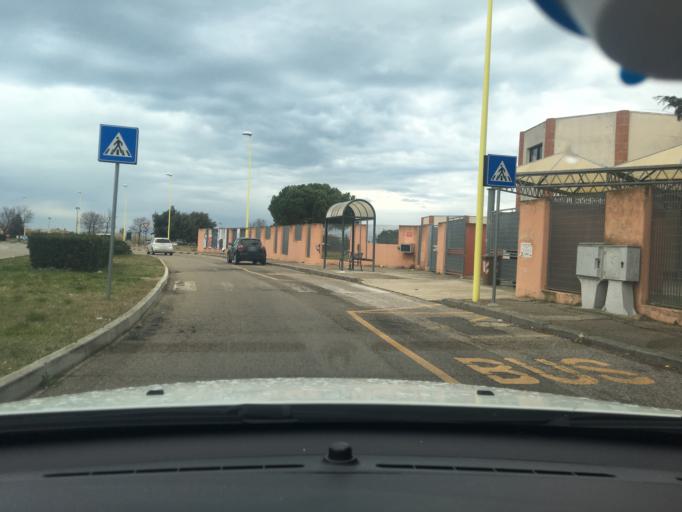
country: IT
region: Molise
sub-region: Provincia di Campobasso
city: Termoli
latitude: 41.9713
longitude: 14.9937
